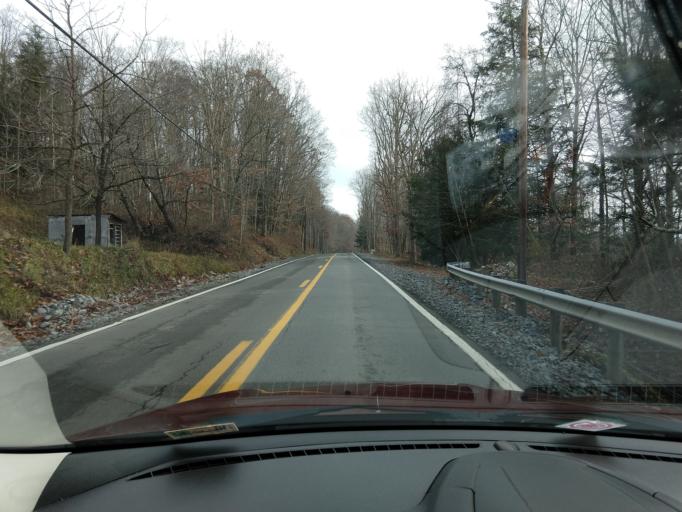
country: US
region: West Virginia
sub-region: Greenbrier County
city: Rainelle
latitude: 38.1000
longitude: -80.6967
